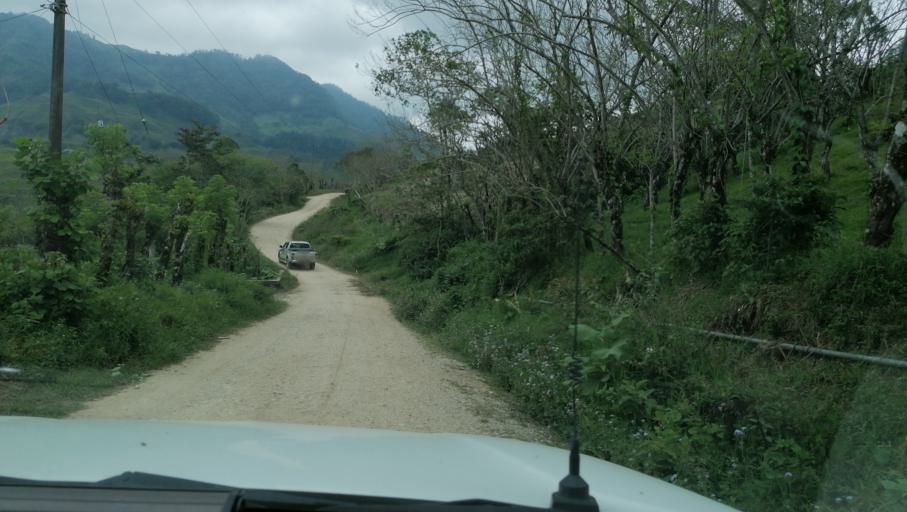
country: MX
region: Chiapas
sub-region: Ocotepec
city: San Pablo Huacano
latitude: 17.2676
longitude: -93.2541
